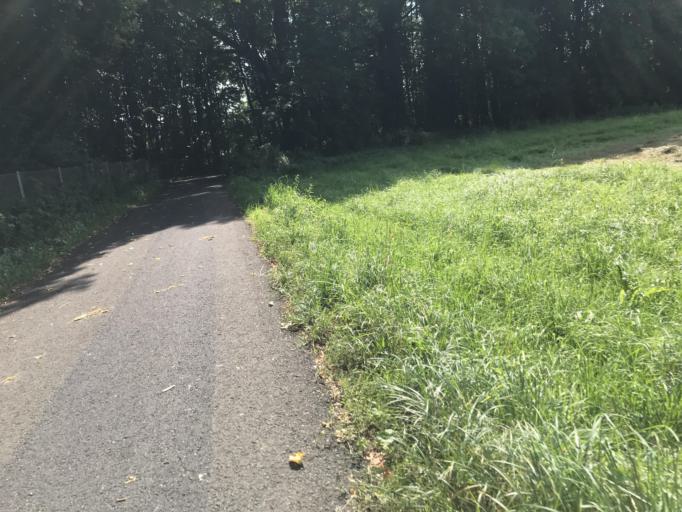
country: DE
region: Hesse
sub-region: Regierungsbezirk Giessen
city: Hungen
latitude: 50.4618
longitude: 8.9116
